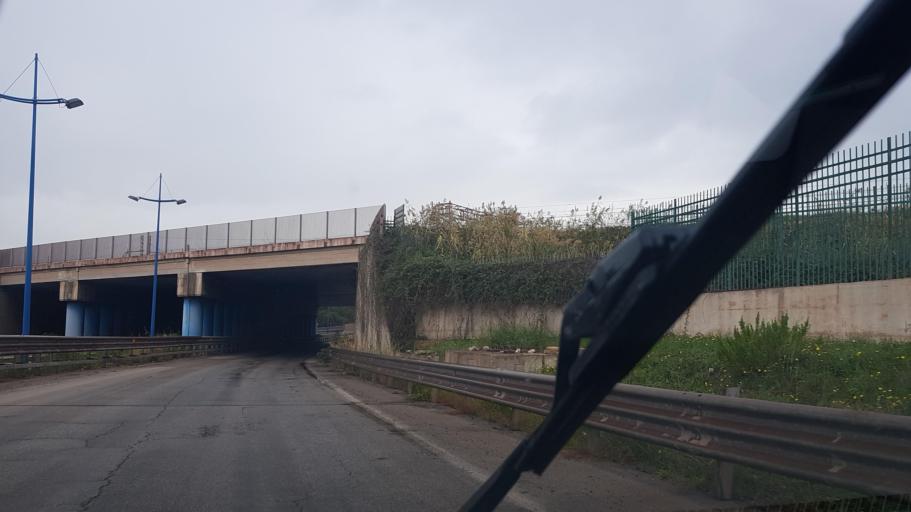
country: IT
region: Apulia
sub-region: Provincia di Taranto
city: Statte
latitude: 40.4815
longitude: 17.2070
